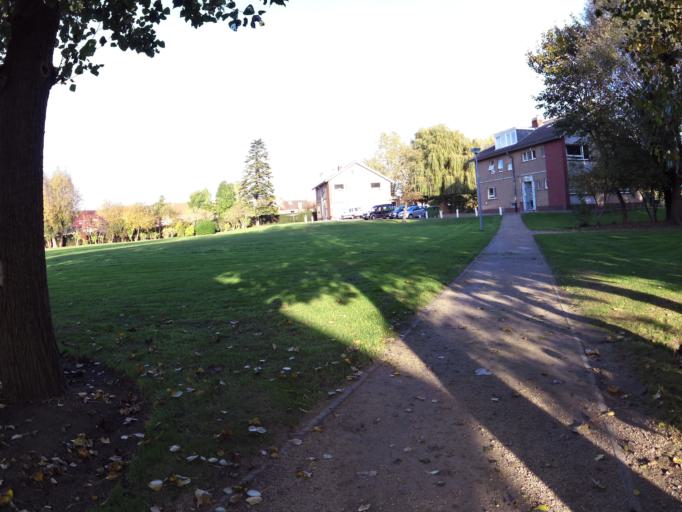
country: BE
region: Flanders
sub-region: Provincie West-Vlaanderen
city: Veurne
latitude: 51.0760
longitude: 2.6593
